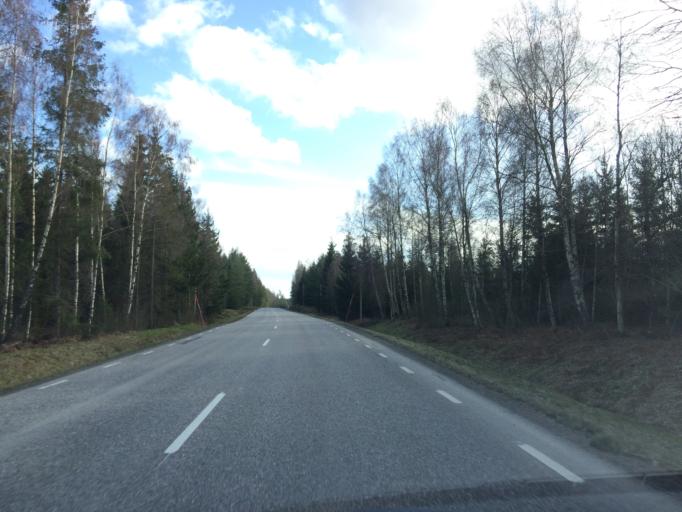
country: SE
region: Kronoberg
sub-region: Almhults Kommun
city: AElmhult
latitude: 56.5896
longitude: 14.0977
